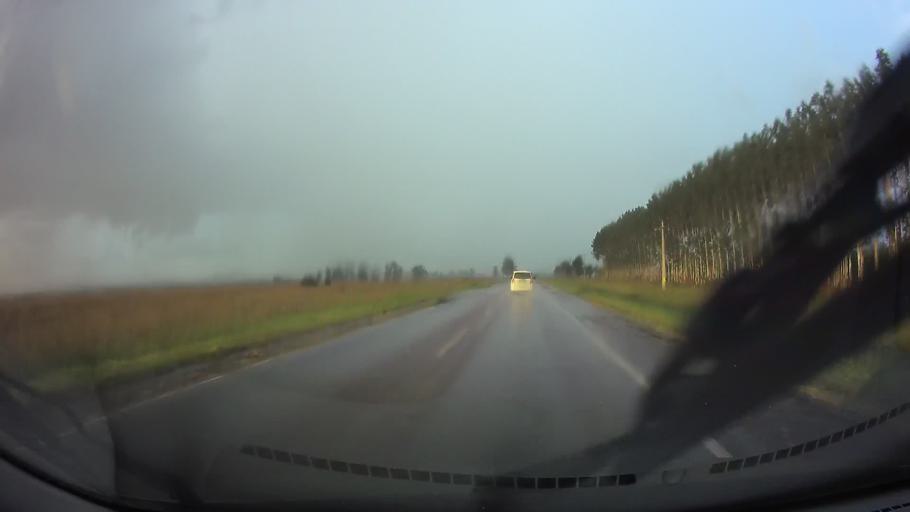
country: PY
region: Paraguari
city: Paraguari
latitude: -25.6645
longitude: -57.1630
